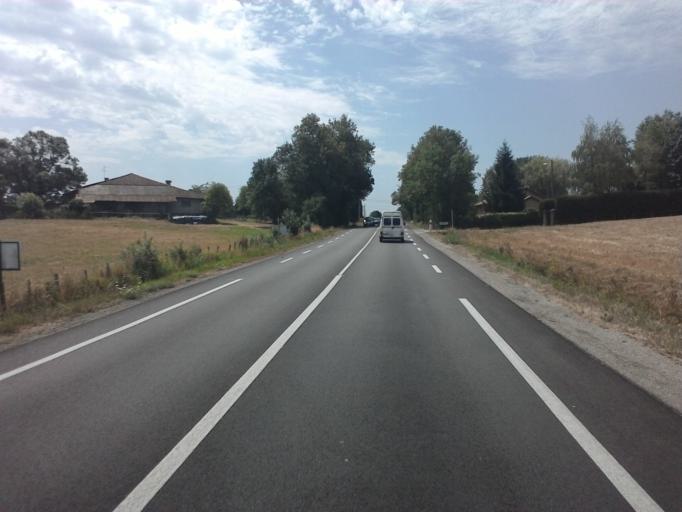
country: FR
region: Rhone-Alpes
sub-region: Departement de l'Ain
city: Saint-Etienne-du-Bois
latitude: 46.2798
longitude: 5.2877
